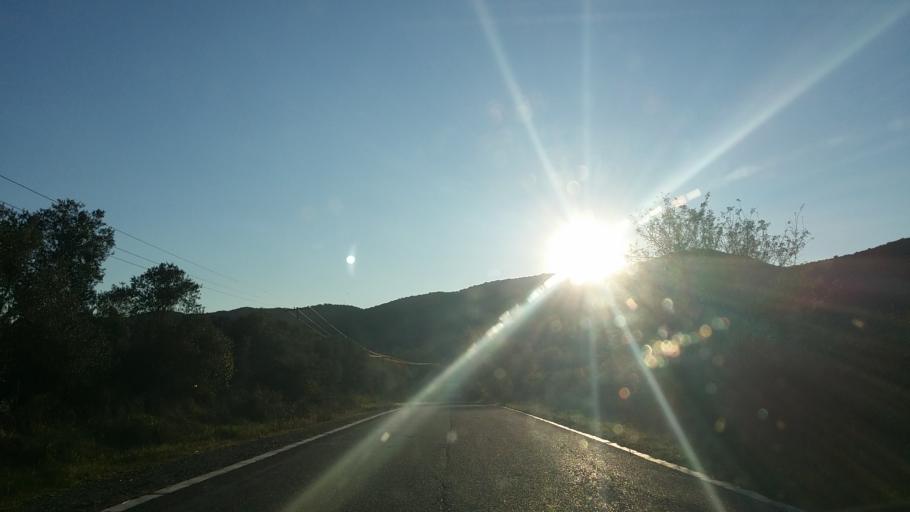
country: GR
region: West Greece
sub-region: Nomos Aitolias kai Akarnanias
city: Lepenou
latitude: 38.7349
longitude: 21.3393
